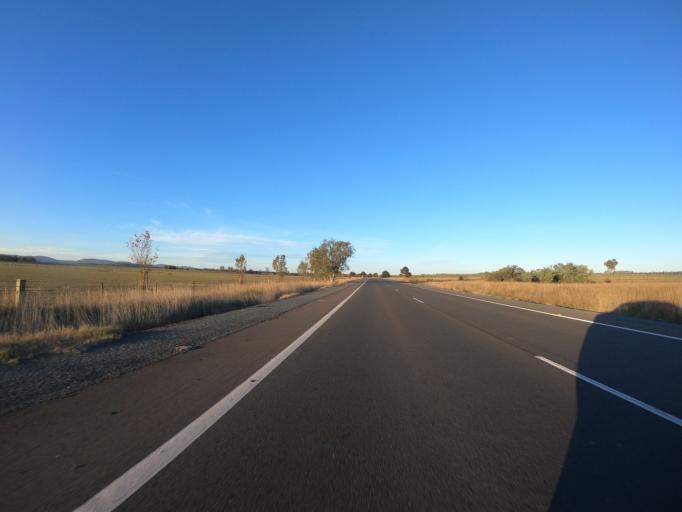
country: AU
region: New South Wales
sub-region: Goulburn Mulwaree
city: Goulburn
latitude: -34.8597
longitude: 149.5496
